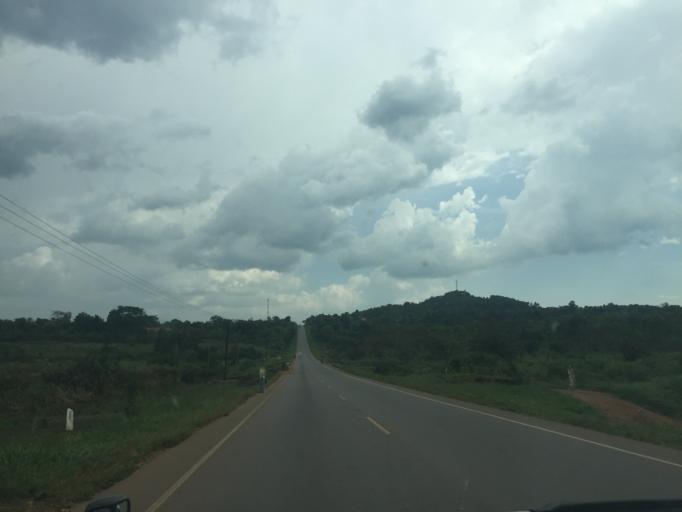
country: UG
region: Central Region
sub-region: Luwero District
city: Wobulenzi
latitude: 0.6573
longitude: 32.5302
